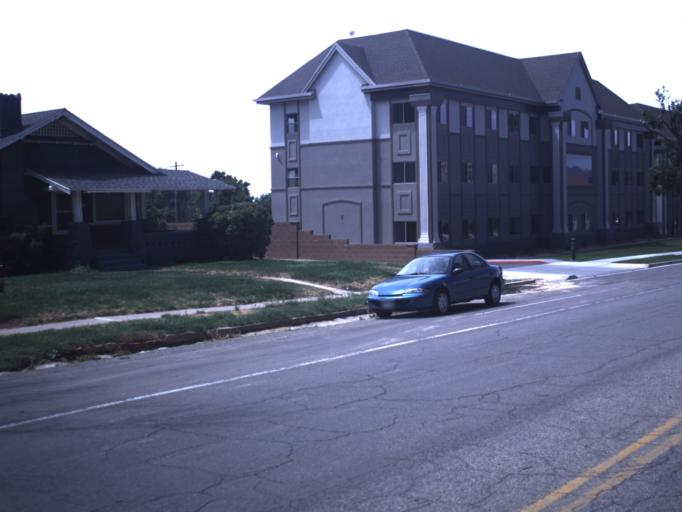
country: US
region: Utah
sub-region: Iron County
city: Cedar City
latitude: 37.6795
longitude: -113.0669
